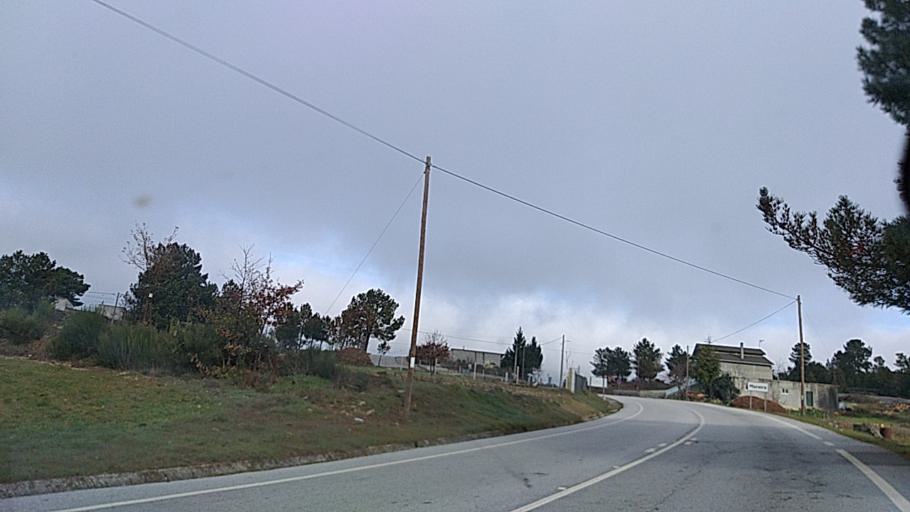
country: PT
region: Guarda
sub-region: Aguiar da Beira
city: Aguiar da Beira
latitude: 40.7383
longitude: -7.4938
